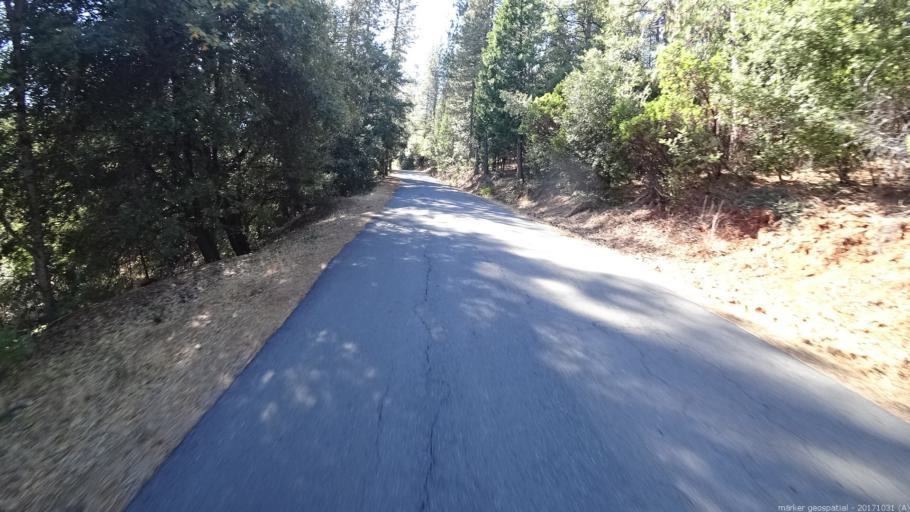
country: US
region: California
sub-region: Shasta County
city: Shingletown
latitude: 40.5242
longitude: -121.9303
